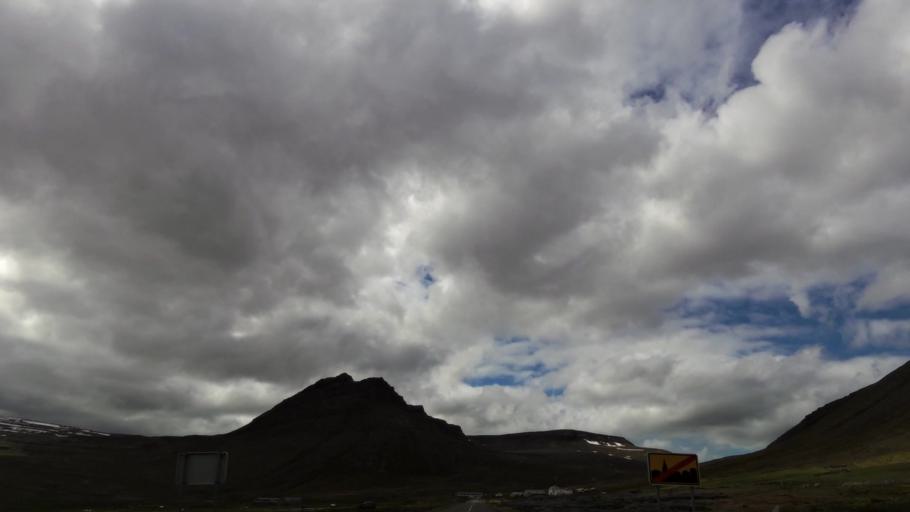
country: IS
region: Westfjords
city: Isafjoerdur
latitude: 66.1588
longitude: -23.2689
